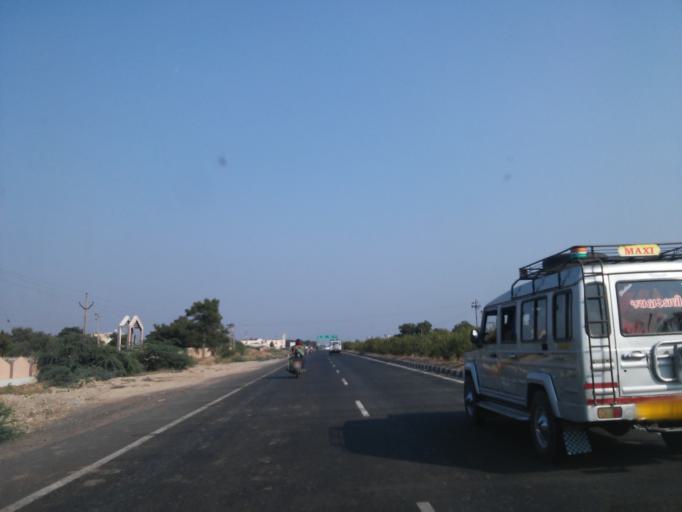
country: IN
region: Gujarat
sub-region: Surendranagar
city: Halvad
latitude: 23.0045
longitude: 71.1588
